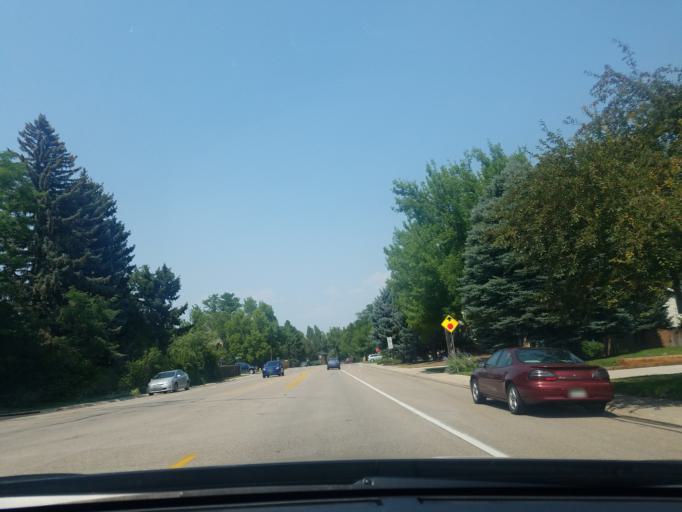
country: US
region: Colorado
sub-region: Larimer County
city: Fort Collins
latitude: 40.5569
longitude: -105.0675
